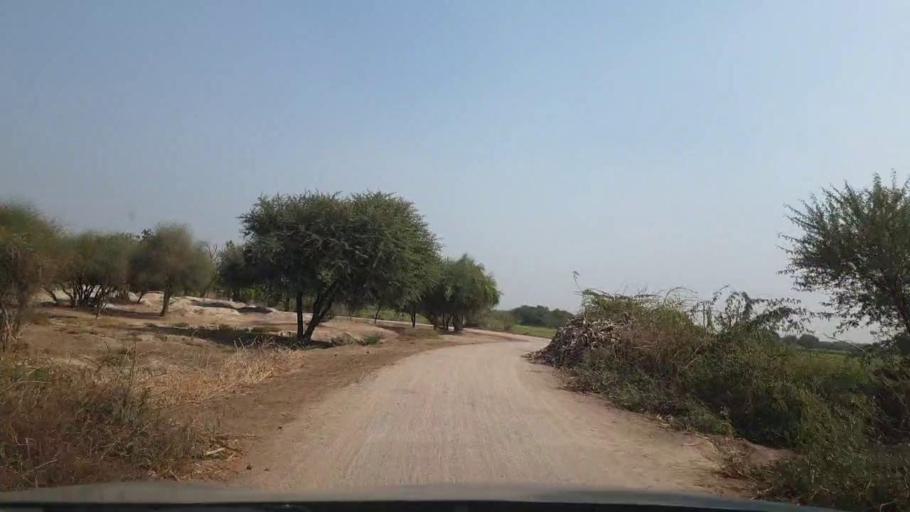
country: PK
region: Sindh
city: Tando Allahyar
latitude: 25.5591
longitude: 68.8410
